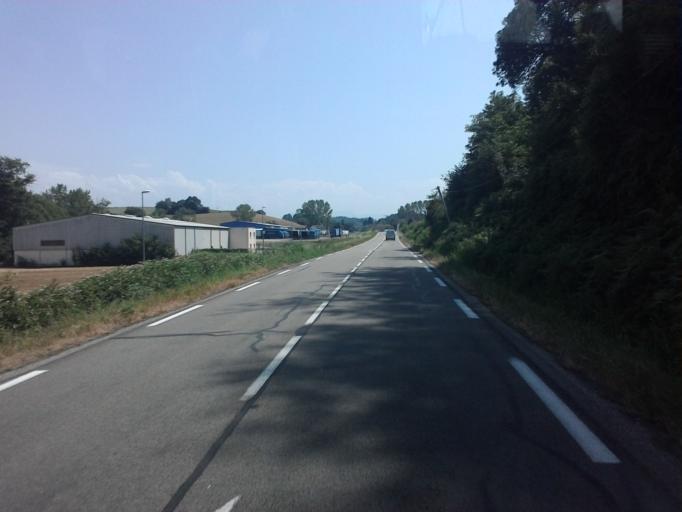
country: FR
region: Rhone-Alpes
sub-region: Departement de l'Isere
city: Faverges-de-la-Tour
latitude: 45.5918
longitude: 5.5384
